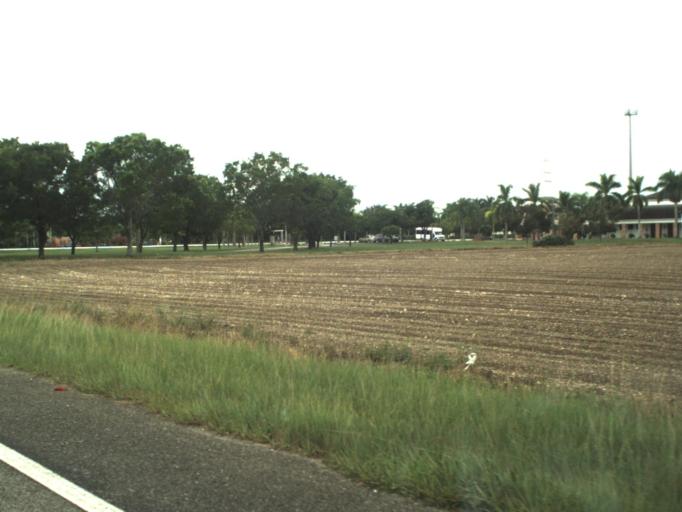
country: US
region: Florida
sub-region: Miami-Dade County
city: Homestead
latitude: 25.4978
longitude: -80.4777
